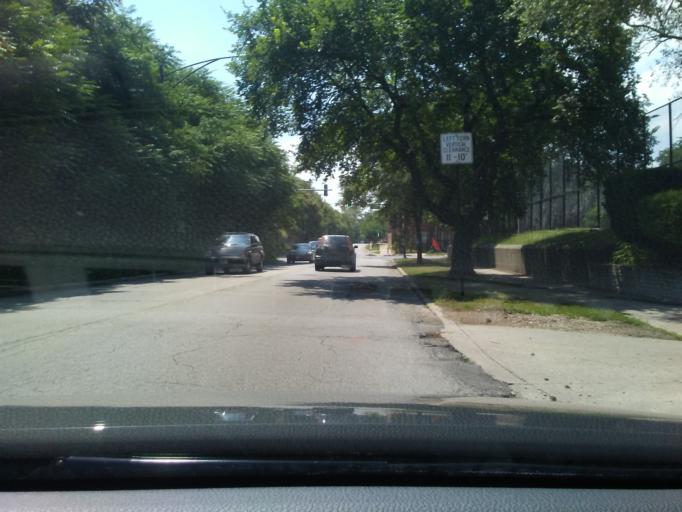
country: US
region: Illinois
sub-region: Cook County
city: Evanston
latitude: 41.9949
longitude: -87.6755
